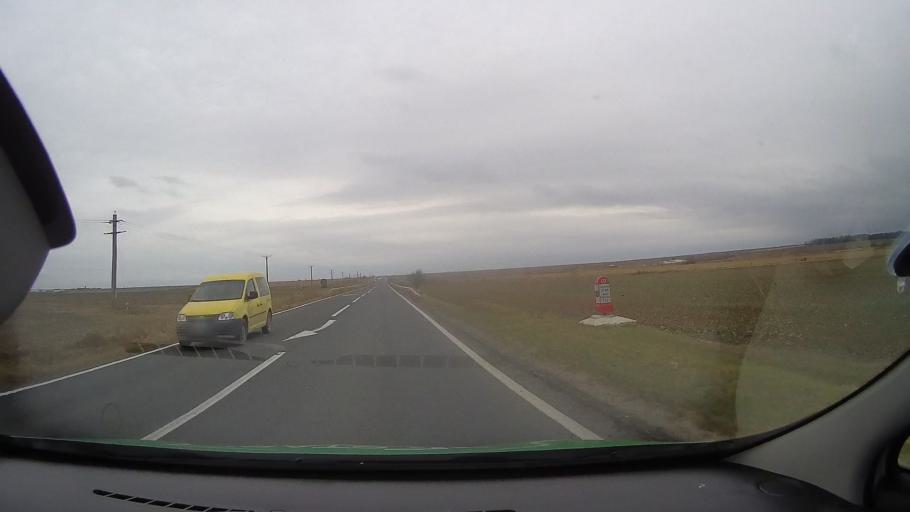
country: RO
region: Constanta
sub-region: Comuna Nicolae Balcescu
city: Nicolae Balcescu
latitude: 44.3868
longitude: 28.3882
